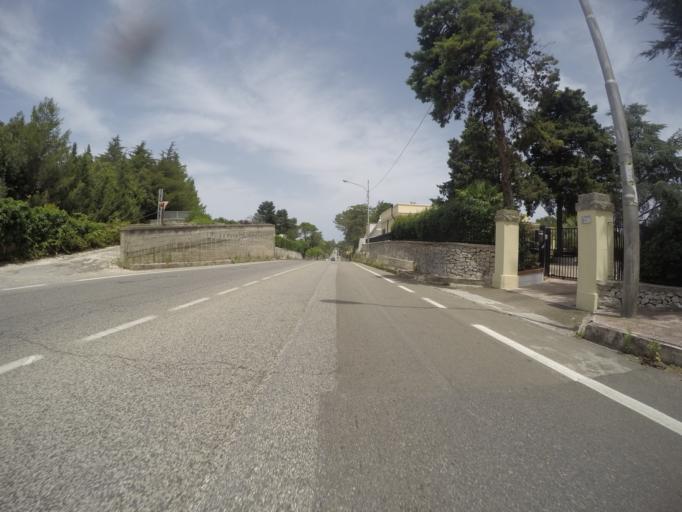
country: IT
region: Apulia
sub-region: Provincia di Taranto
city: Martina Franca
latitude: 40.6877
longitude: 17.3333
